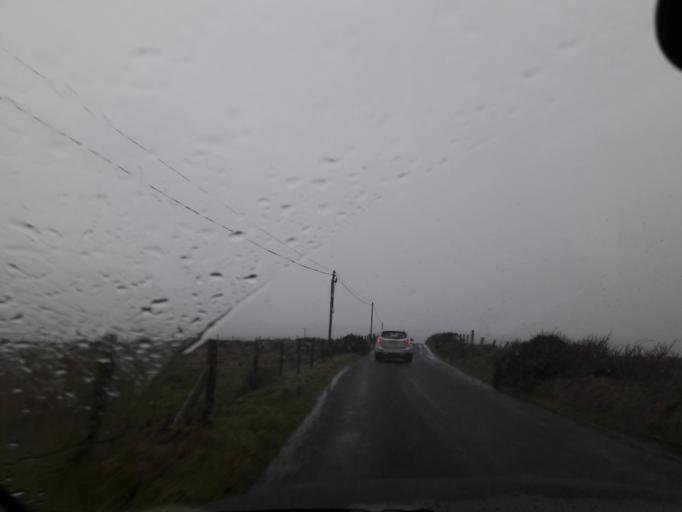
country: IE
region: Ulster
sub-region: County Donegal
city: Buncrana
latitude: 55.2741
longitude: -7.6387
